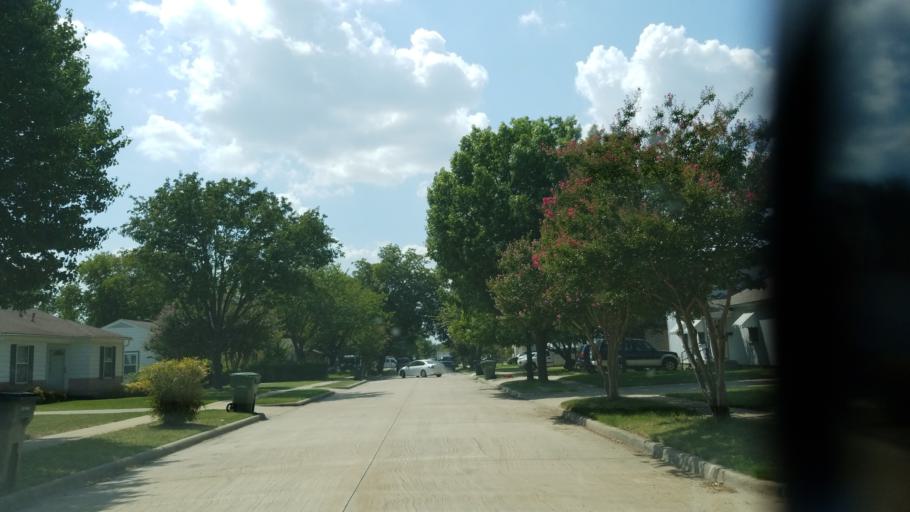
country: US
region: Texas
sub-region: Dallas County
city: Garland
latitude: 32.9189
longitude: -96.6466
